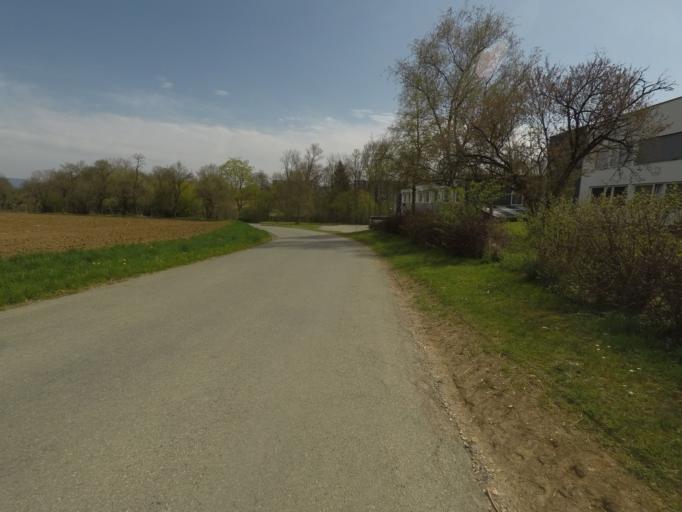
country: DE
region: Baden-Wuerttemberg
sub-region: Tuebingen Region
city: Wannweil
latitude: 48.4994
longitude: 9.1345
